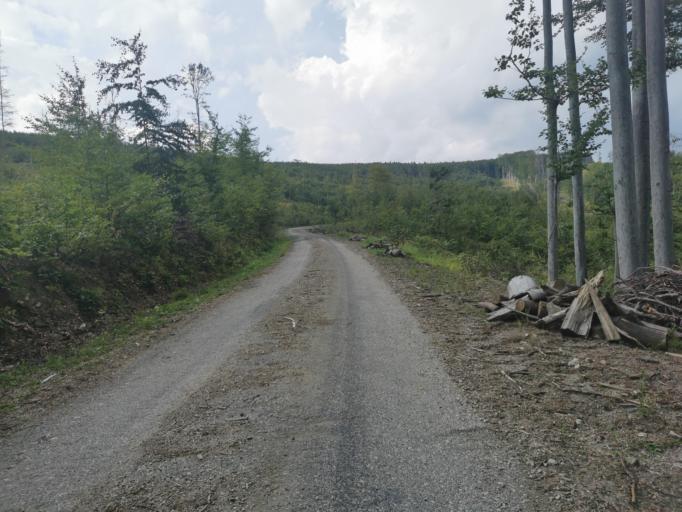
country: SK
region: Nitriansky
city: Stara Tura
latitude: 48.8299
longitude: 17.6241
